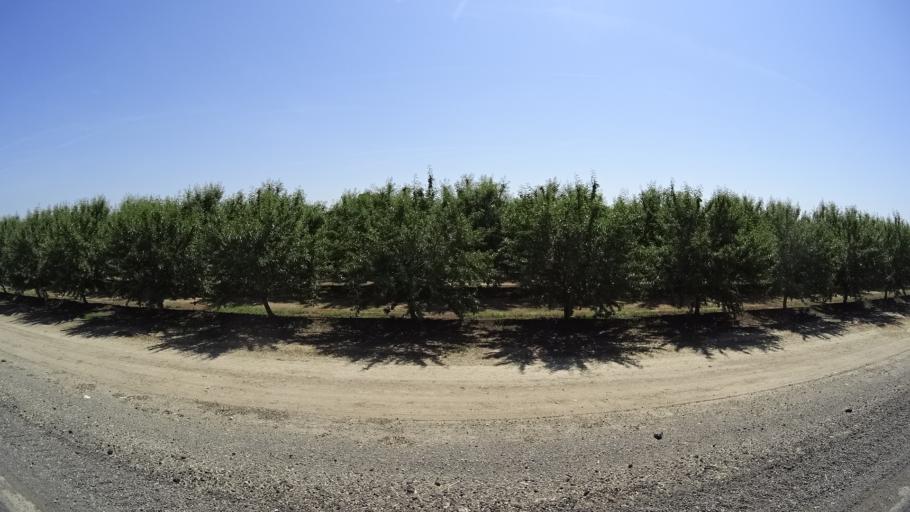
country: US
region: California
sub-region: Fresno County
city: Riverdale
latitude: 36.3544
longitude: -119.8513
